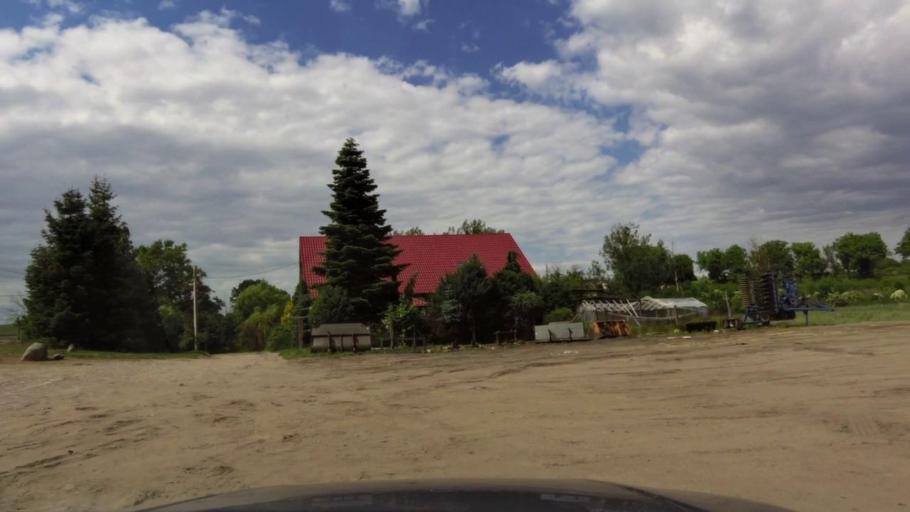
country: PL
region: West Pomeranian Voivodeship
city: Trzcinsko Zdroj
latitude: 52.9107
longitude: 14.5941
